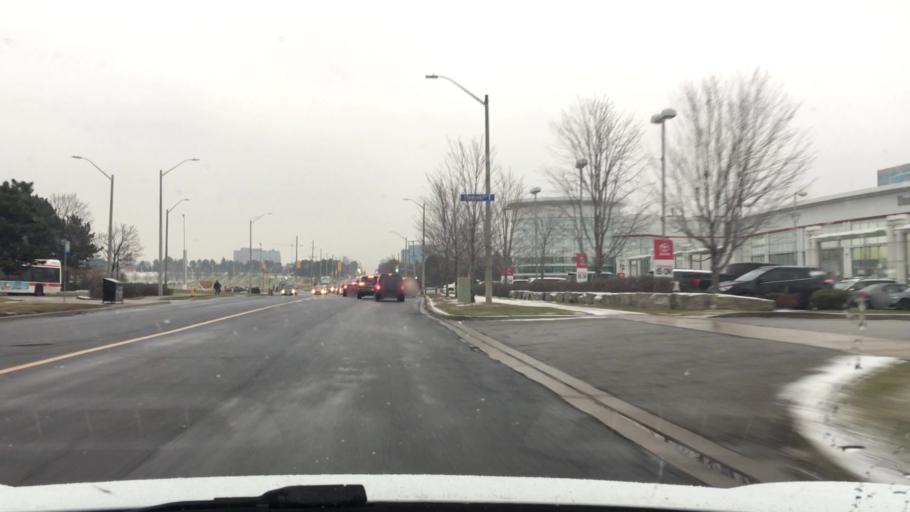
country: CA
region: Ontario
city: Willowdale
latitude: 43.8172
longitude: -79.3421
